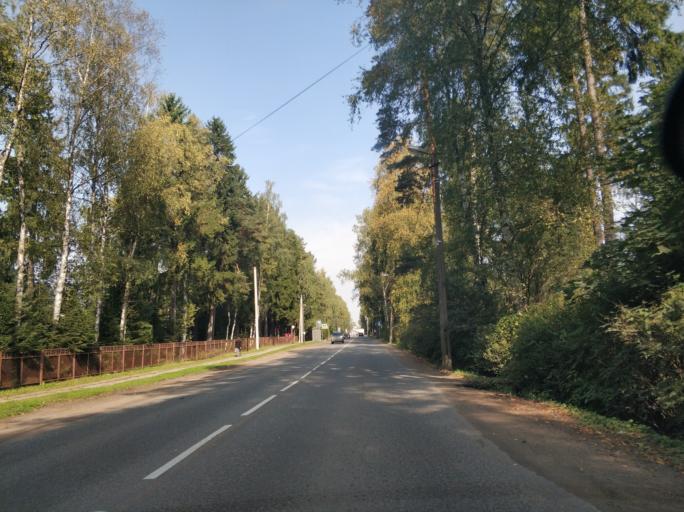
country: RU
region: Leningrad
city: Vsevolozhsk
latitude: 60.0115
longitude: 30.6202
